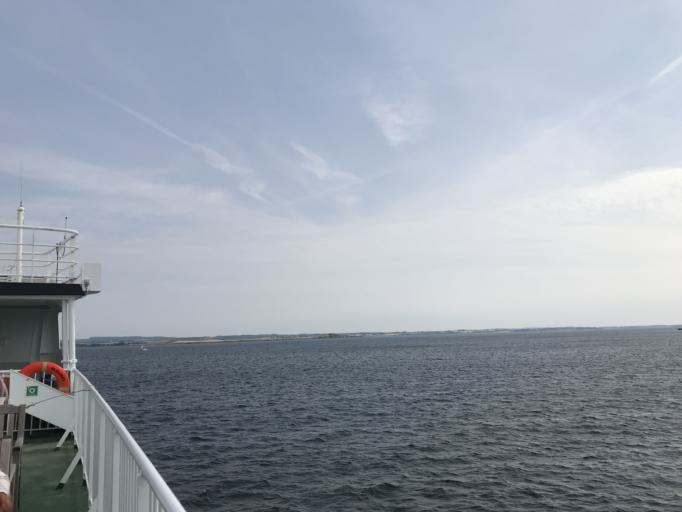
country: DK
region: South Denmark
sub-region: Faaborg-Midtfyn Kommune
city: Faaborg
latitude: 55.0387
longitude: 10.2287
